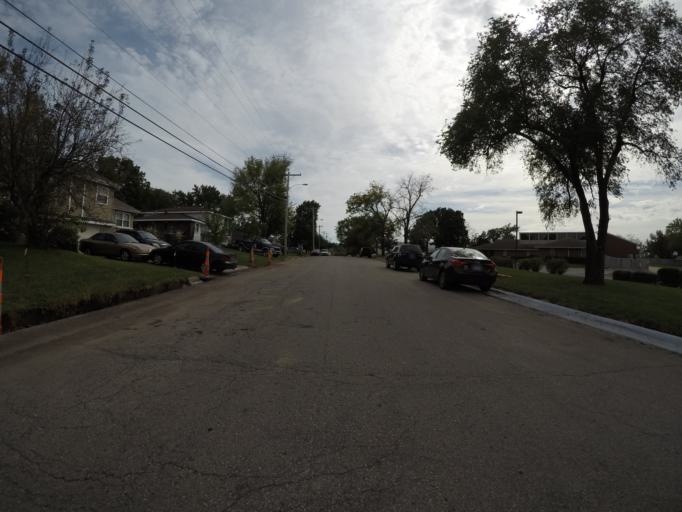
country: US
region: Kansas
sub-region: Johnson County
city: Olathe
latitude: 38.8868
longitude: -94.8299
